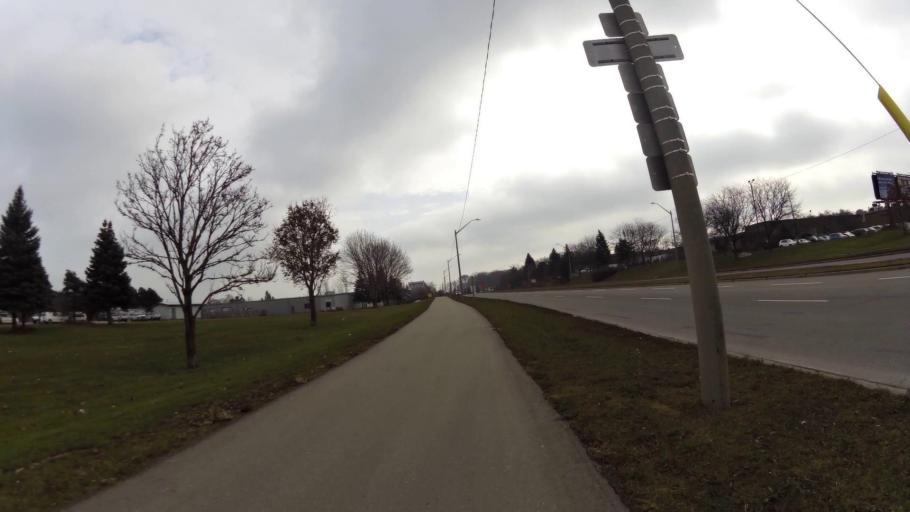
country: CA
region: Ontario
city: Kitchener
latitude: 43.4258
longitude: -80.4801
